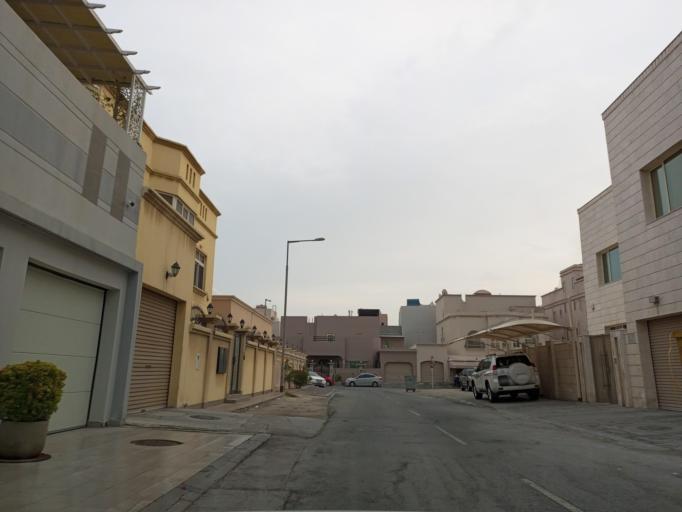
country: BH
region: Muharraq
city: Al Hadd
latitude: 26.2457
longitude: 50.6432
